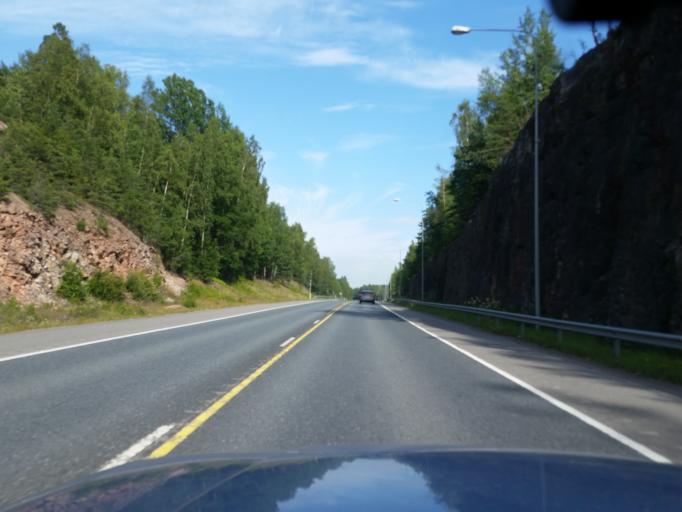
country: FI
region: Uusimaa
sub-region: Helsinki
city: Siuntio
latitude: 60.0964
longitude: 24.2642
